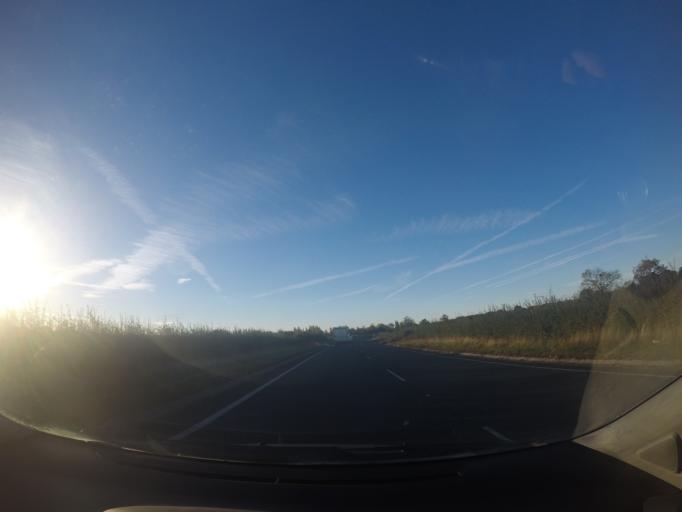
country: GB
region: England
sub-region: City of York
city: Copmanthorpe
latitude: 53.9289
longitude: -1.1441
